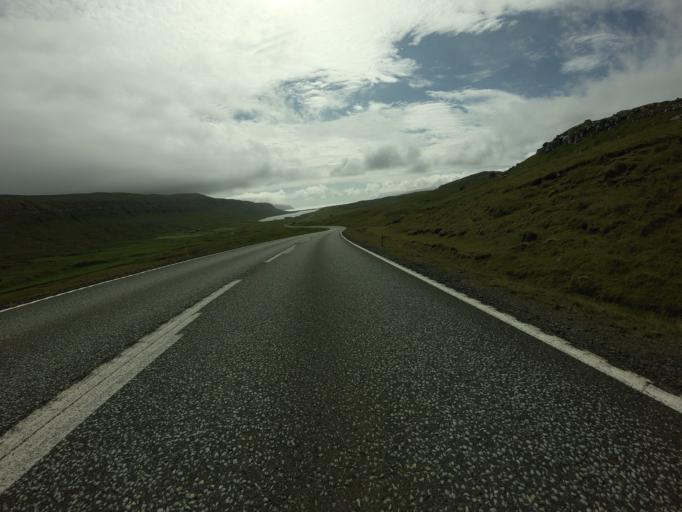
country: FO
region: Sandoy
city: Sandur
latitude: 61.8690
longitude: -6.8447
